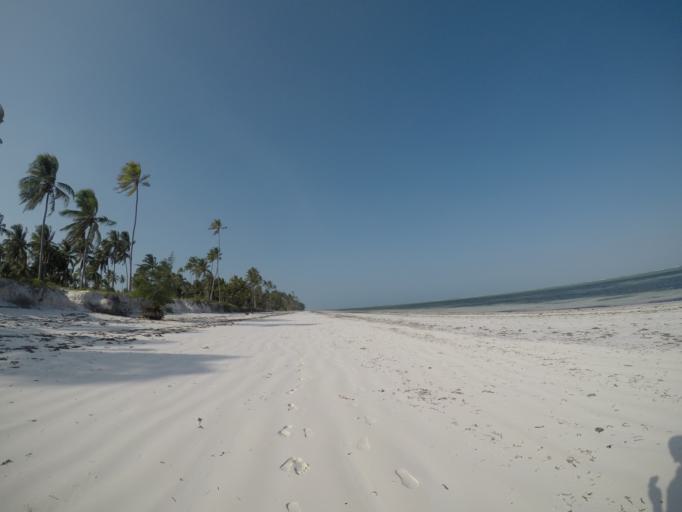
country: TZ
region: Zanzibar Central/South
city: Nganane
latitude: -6.2110
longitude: 39.5343
